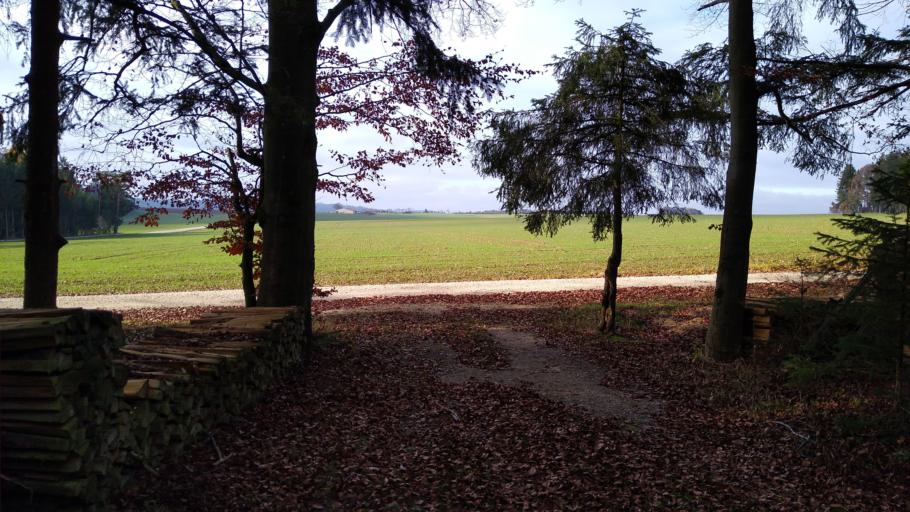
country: DE
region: Bavaria
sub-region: Upper Palatinate
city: Seubersdorf
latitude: 49.1328
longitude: 11.6326
